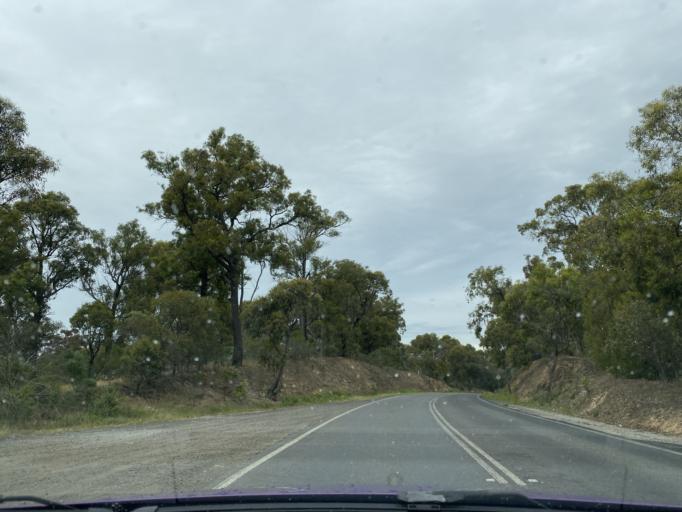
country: AU
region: Victoria
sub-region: Nillumbik
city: Diamond Creek
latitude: -37.6479
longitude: 145.1478
